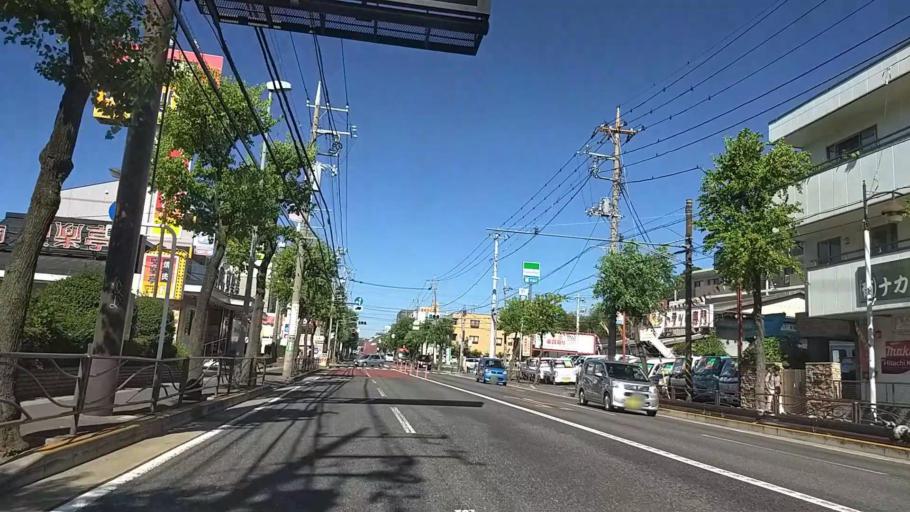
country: JP
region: Tokyo
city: Chofugaoka
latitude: 35.5851
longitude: 139.5792
